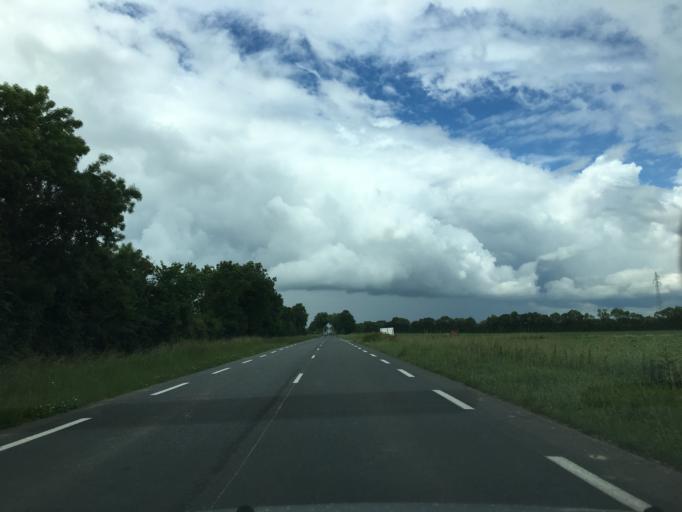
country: FR
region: Poitou-Charentes
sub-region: Departement de la Charente-Maritime
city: Saint-Jean-d'Angely
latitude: 46.0564
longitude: -0.5094
